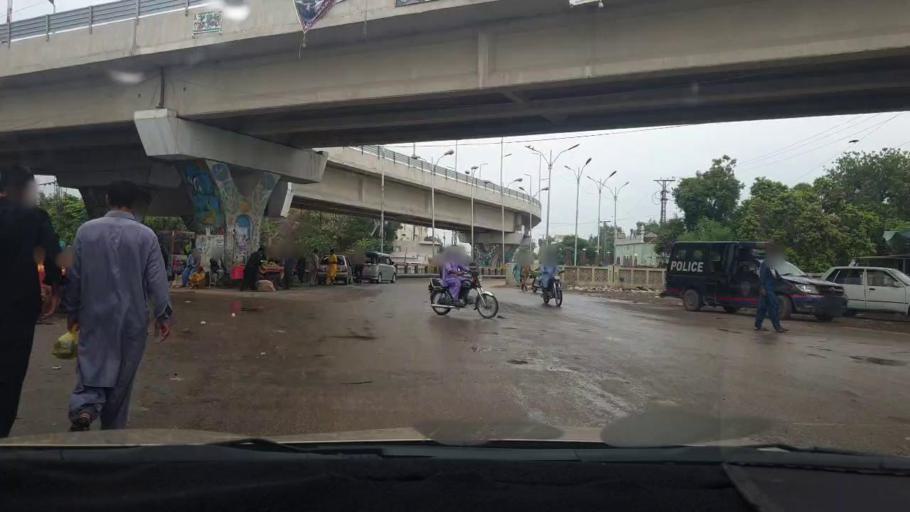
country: PK
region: Sindh
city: Larkana
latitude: 27.5610
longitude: 68.2071
